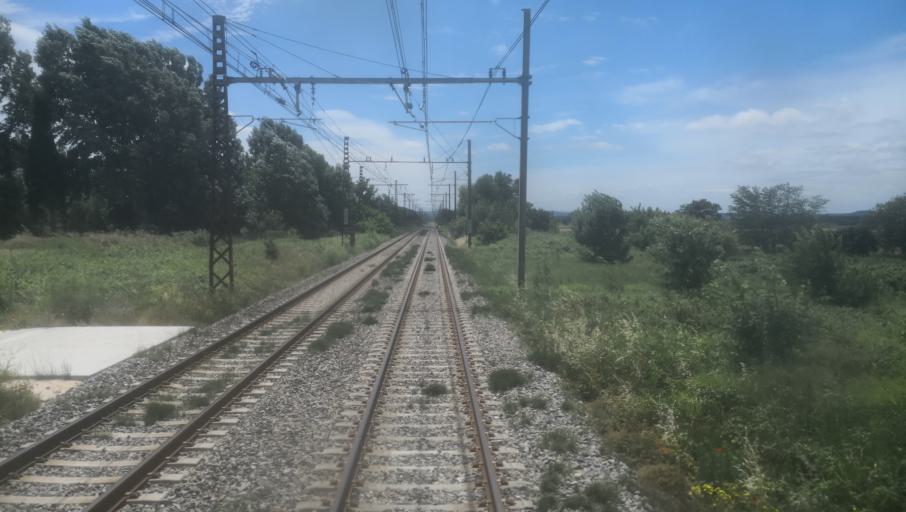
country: FR
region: Languedoc-Roussillon
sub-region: Departement de l'Aude
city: Coursan
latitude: 43.2324
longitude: 3.0494
